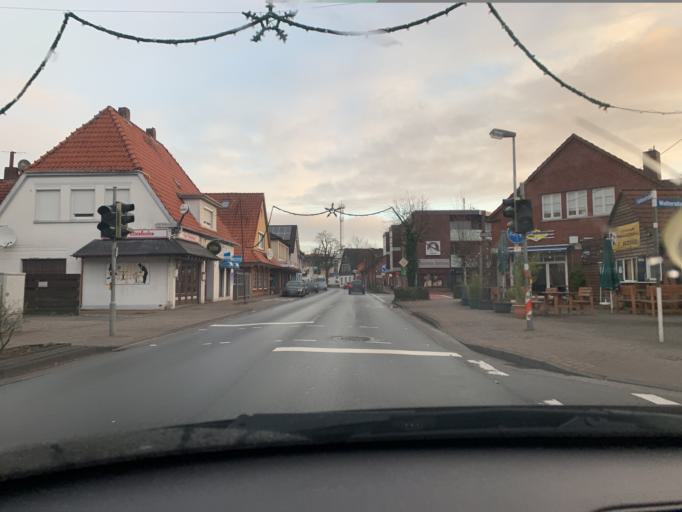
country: DE
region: Lower Saxony
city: Westerstede
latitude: 53.2556
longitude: 7.9218
